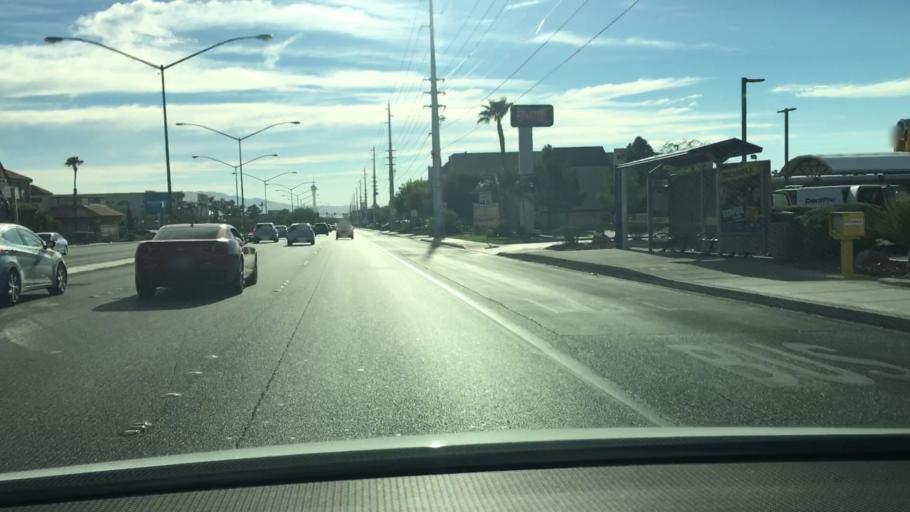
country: US
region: Nevada
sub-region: Clark County
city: Spring Valley
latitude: 36.1440
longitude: -115.2346
